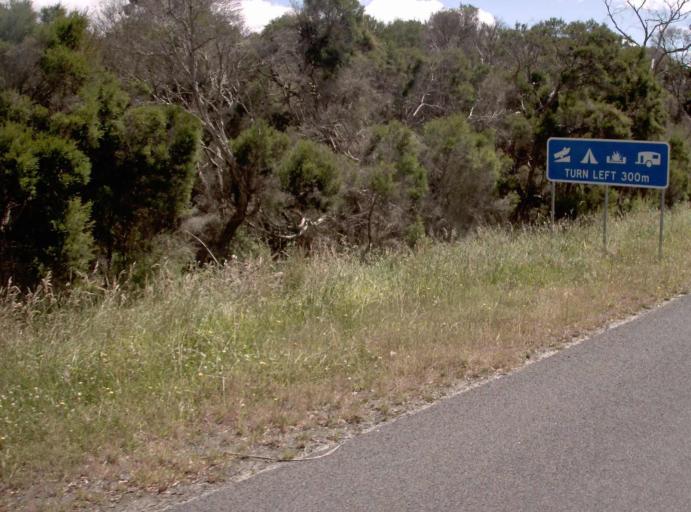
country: AU
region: Victoria
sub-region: Bass Coast
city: North Wonthaggi
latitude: -38.4348
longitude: 145.4932
